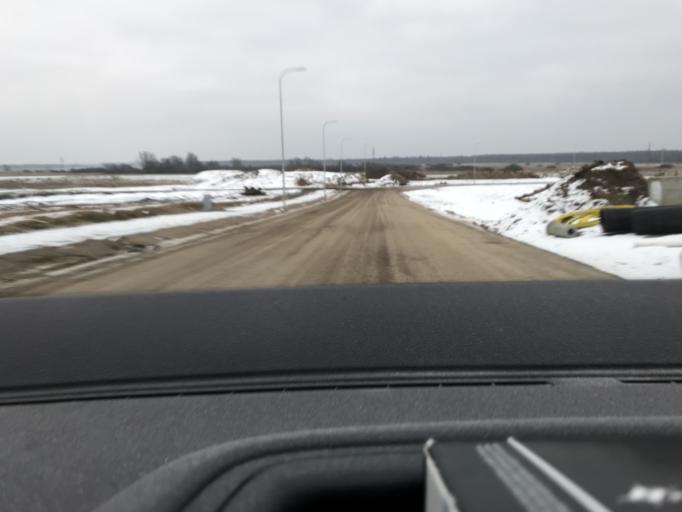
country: SE
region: Skane
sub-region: Ystads Kommun
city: Ystad
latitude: 55.4497
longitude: 13.8540
